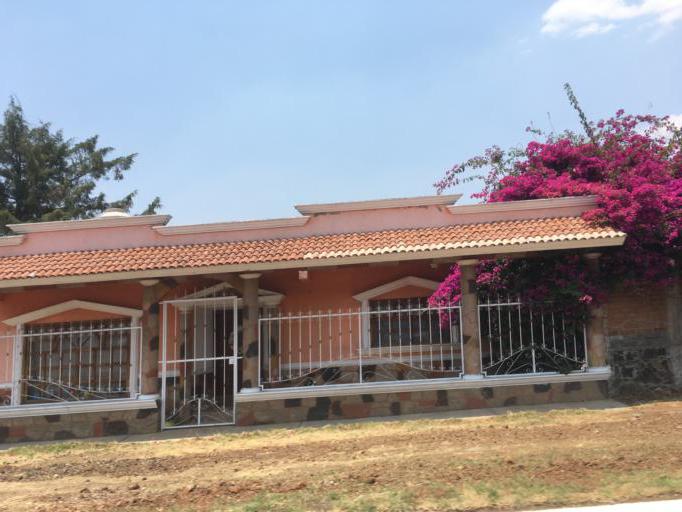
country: MX
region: Michoacan
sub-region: Morelia
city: Iratzio
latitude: 19.6321
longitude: -101.4686
